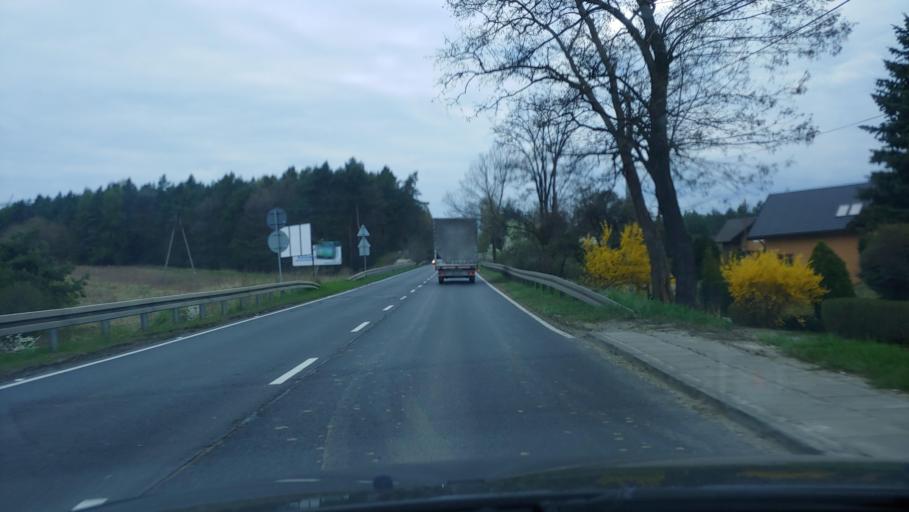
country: PL
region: Silesian Voivodeship
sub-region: Jaworzno
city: Jaworzno
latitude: 50.1671
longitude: 19.3019
